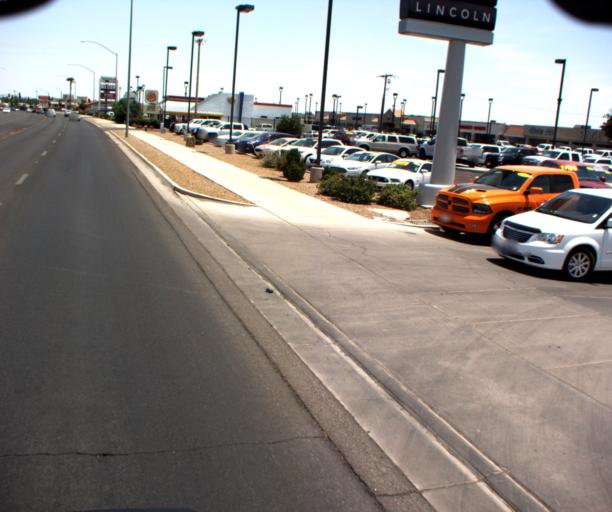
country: US
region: Arizona
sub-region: Graham County
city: Thatcher
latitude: 32.8377
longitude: -109.7353
